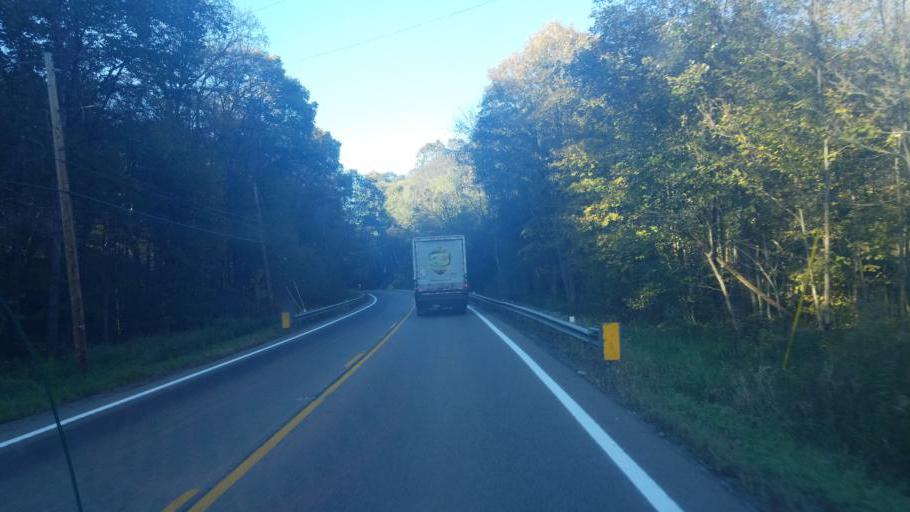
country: US
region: Ohio
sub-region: Columbiana County
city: Glenmoor
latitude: 40.7375
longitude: -80.6388
